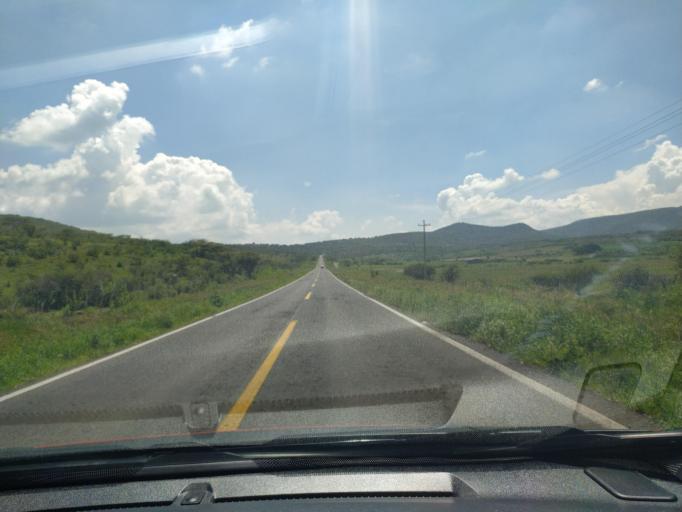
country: MX
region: Guanajuato
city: Ciudad Manuel Doblado
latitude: 20.6330
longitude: -101.9745
